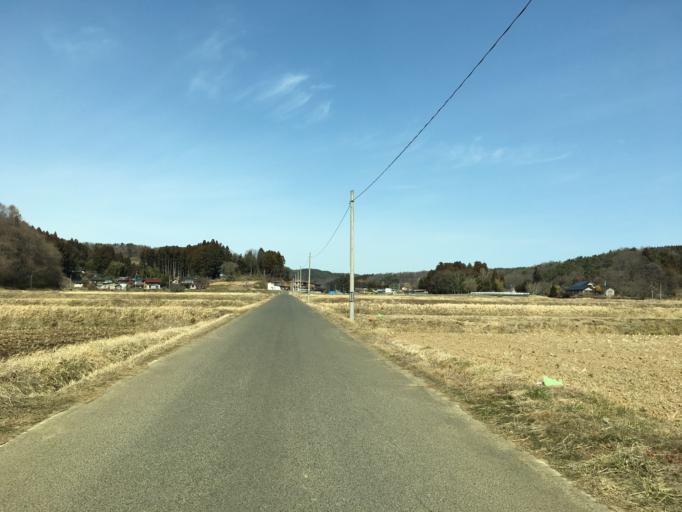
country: JP
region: Fukushima
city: Nihommatsu
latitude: 37.5860
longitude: 140.3870
